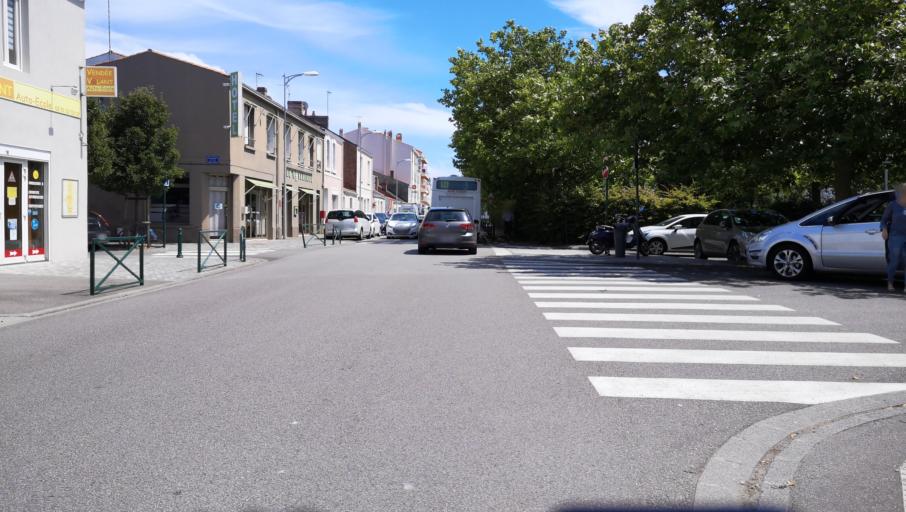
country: FR
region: Pays de la Loire
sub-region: Departement de la Vendee
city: Les Sables-d'Olonne
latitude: 46.5008
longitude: -1.7816
